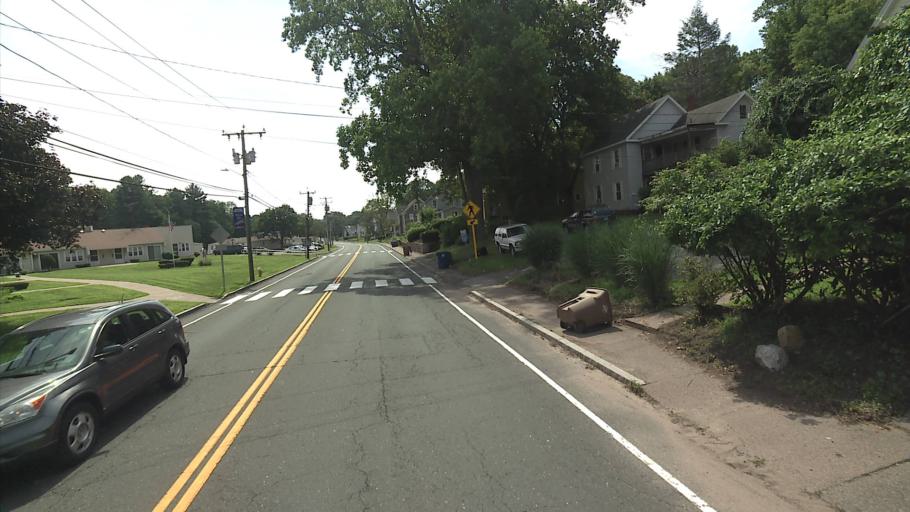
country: US
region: Connecticut
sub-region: Tolland County
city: Rockville
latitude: 41.8645
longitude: -72.4407
